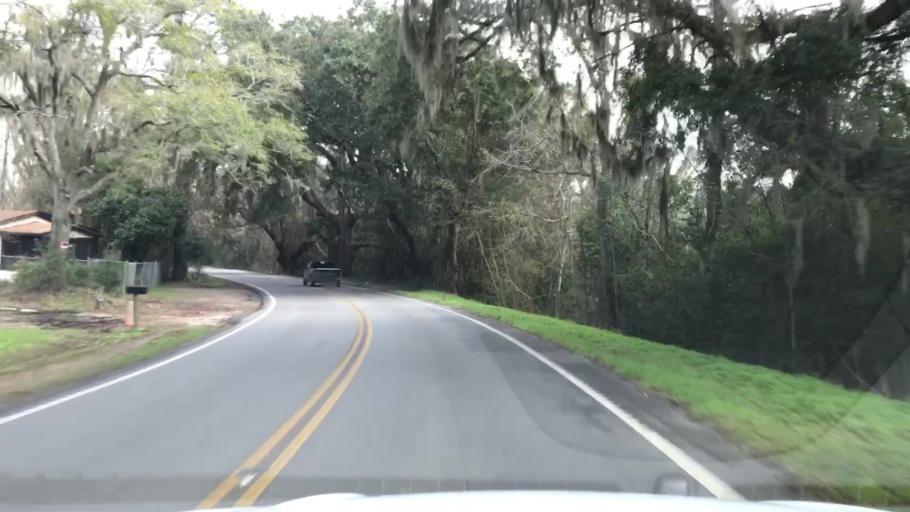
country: US
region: South Carolina
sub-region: Charleston County
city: Kiawah Island
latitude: 32.6782
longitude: -80.0344
